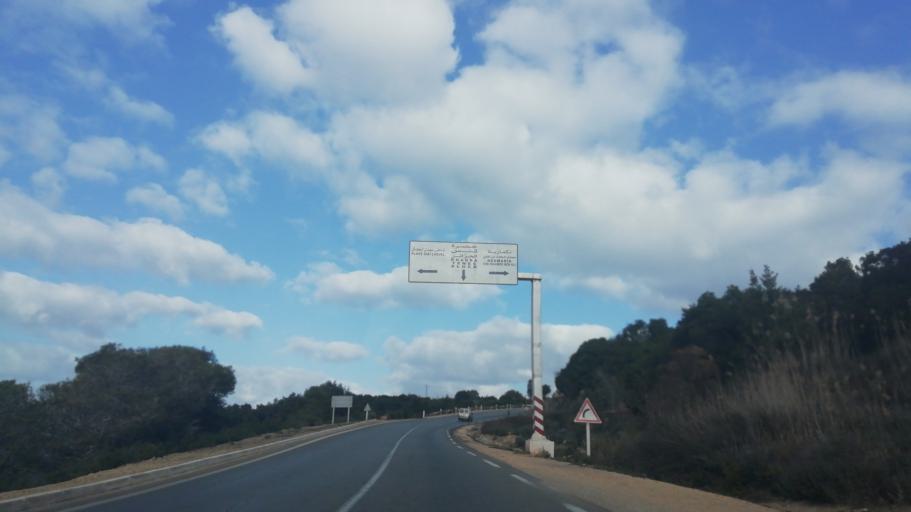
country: DZ
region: Relizane
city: Mazouna
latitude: 36.2420
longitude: 0.5381
